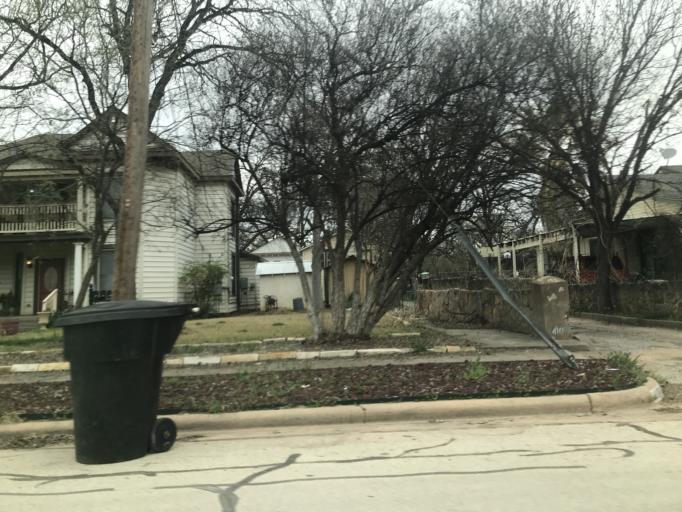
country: US
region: Texas
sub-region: Taylor County
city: Abilene
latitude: 32.4535
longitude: -99.7461
